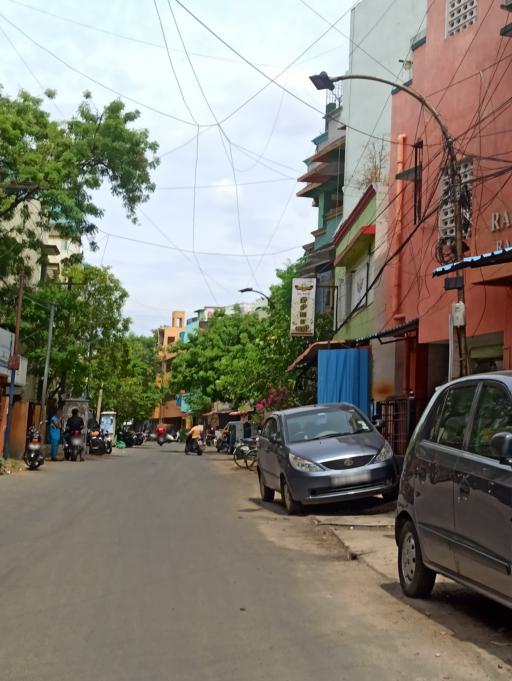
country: IN
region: Tamil Nadu
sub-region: Chennai
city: Chetput
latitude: 13.0583
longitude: 80.2285
